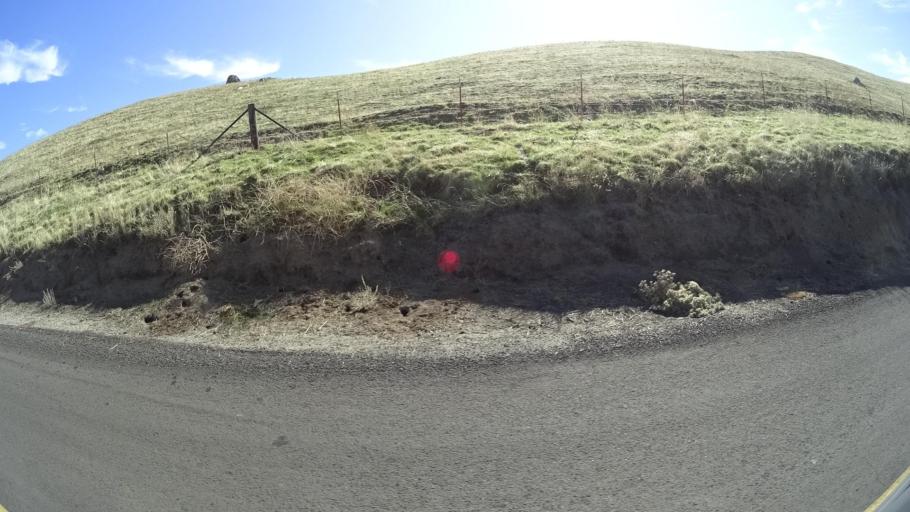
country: US
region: California
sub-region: Tulare County
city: Richgrove
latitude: 35.6837
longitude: -118.8830
